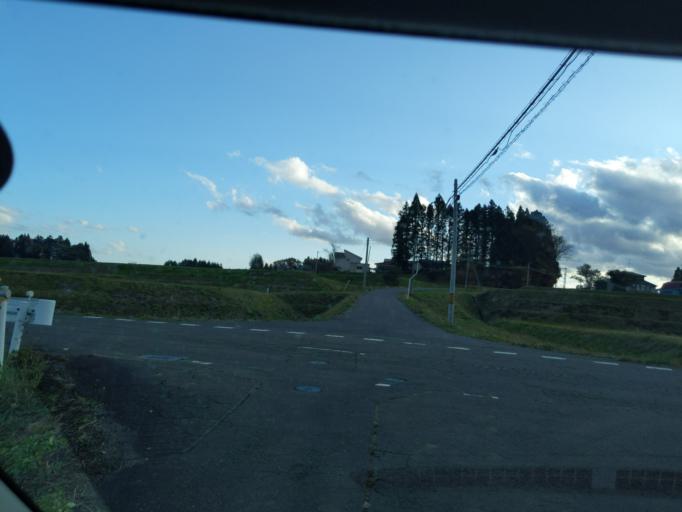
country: JP
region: Iwate
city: Mizusawa
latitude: 39.0942
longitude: 141.0388
